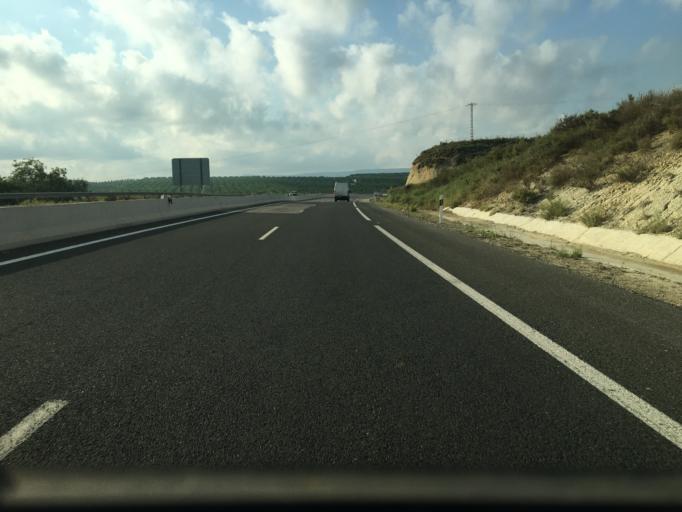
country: ES
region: Murcia
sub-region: Murcia
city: Beniel
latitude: 37.9934
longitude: -0.9769
